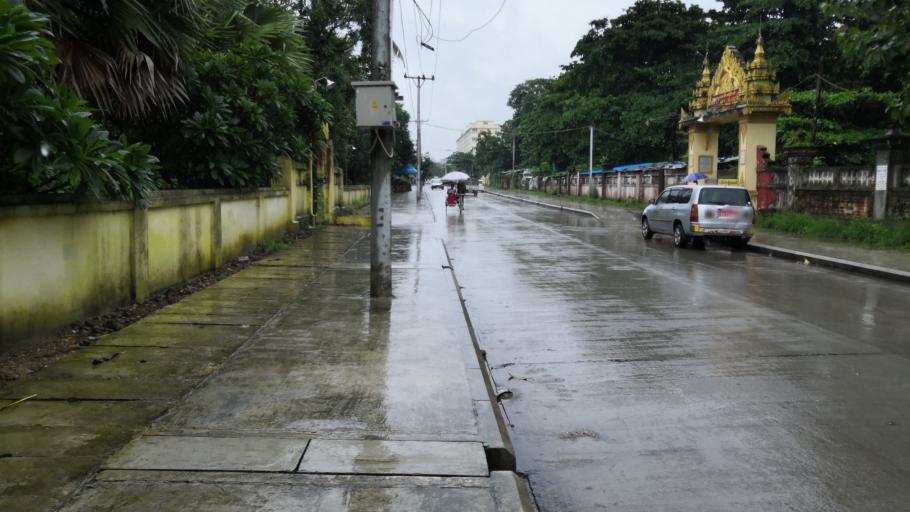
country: MM
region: Yangon
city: Yangon
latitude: 16.8374
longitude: 96.1918
